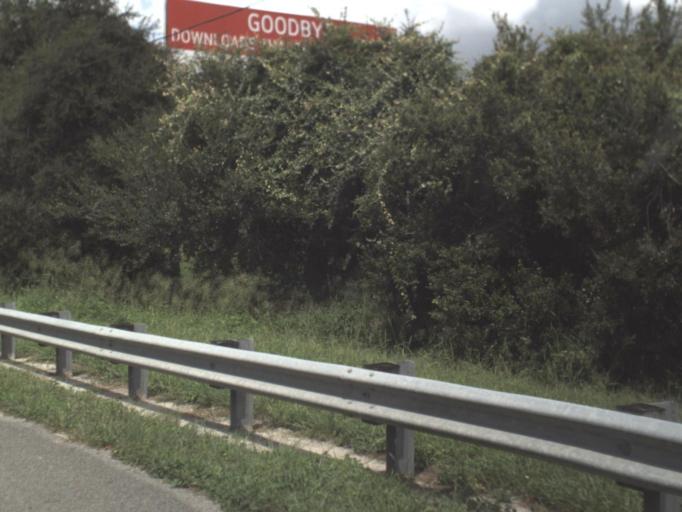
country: US
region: Florida
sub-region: Pasco County
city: Zephyrhills West
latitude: 28.2266
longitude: -82.2307
